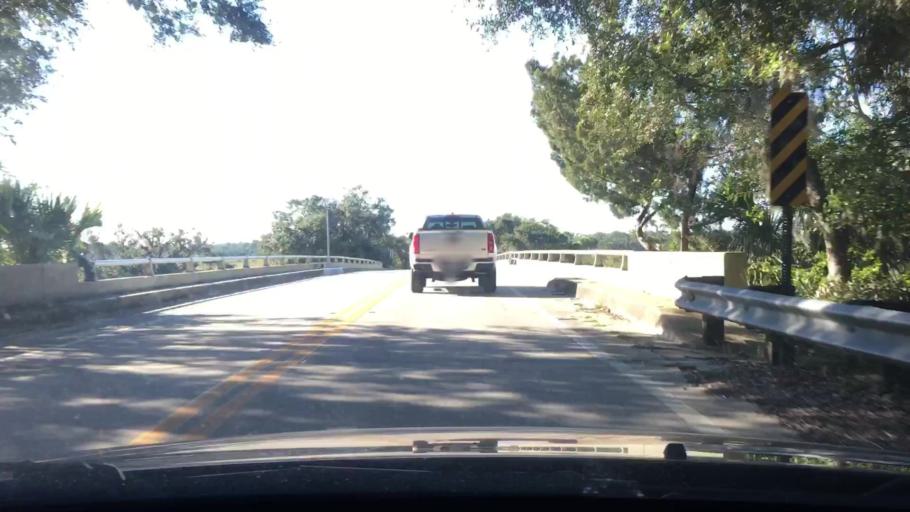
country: US
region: Florida
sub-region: Volusia County
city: Ormond-by-the-Sea
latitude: 29.3423
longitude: -81.0859
